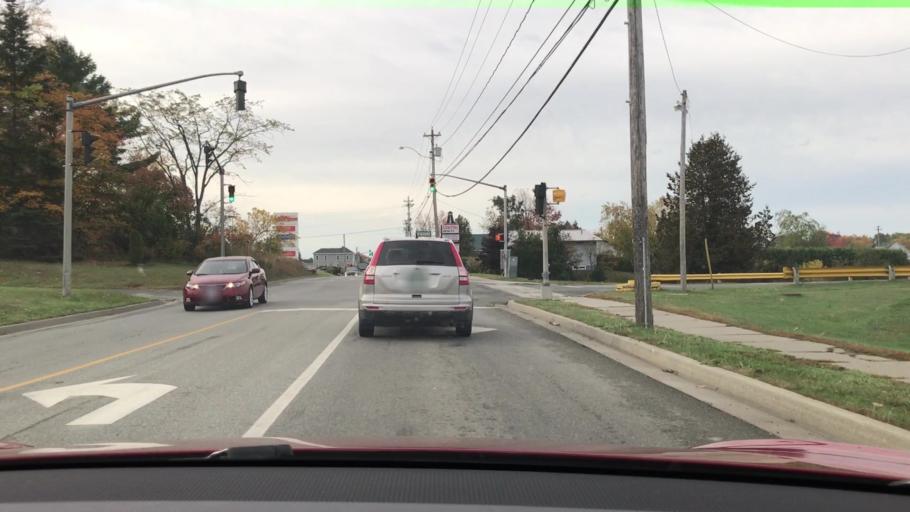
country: US
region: Maine
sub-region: Washington County
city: Calais
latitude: 45.2041
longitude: -67.2726
